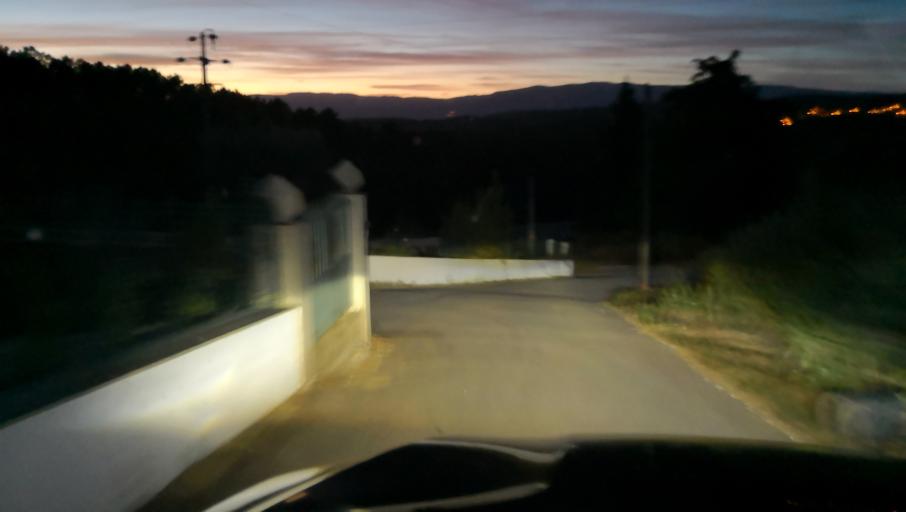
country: PT
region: Vila Real
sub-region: Sabrosa
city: Vilela
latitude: 41.2565
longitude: -7.6554
